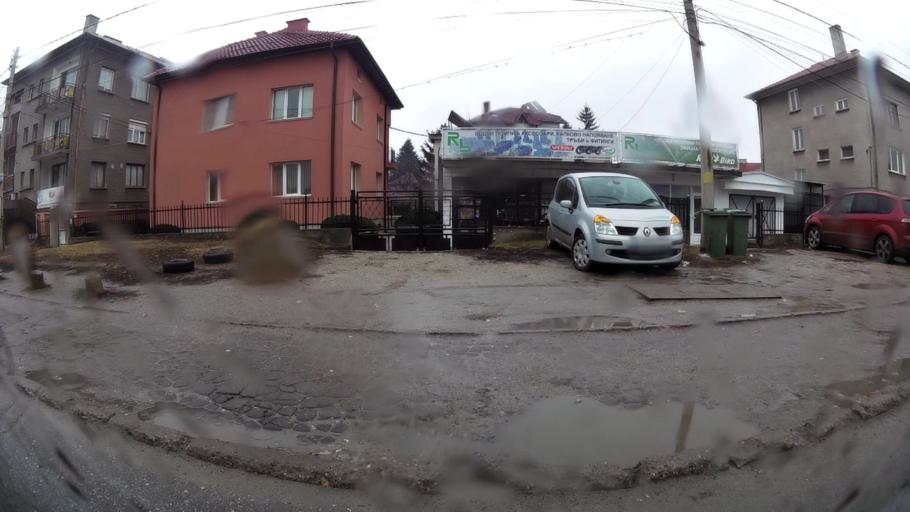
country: BG
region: Sofia-Capital
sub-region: Stolichna Obshtina
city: Sofia
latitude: 42.6367
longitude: 23.4108
